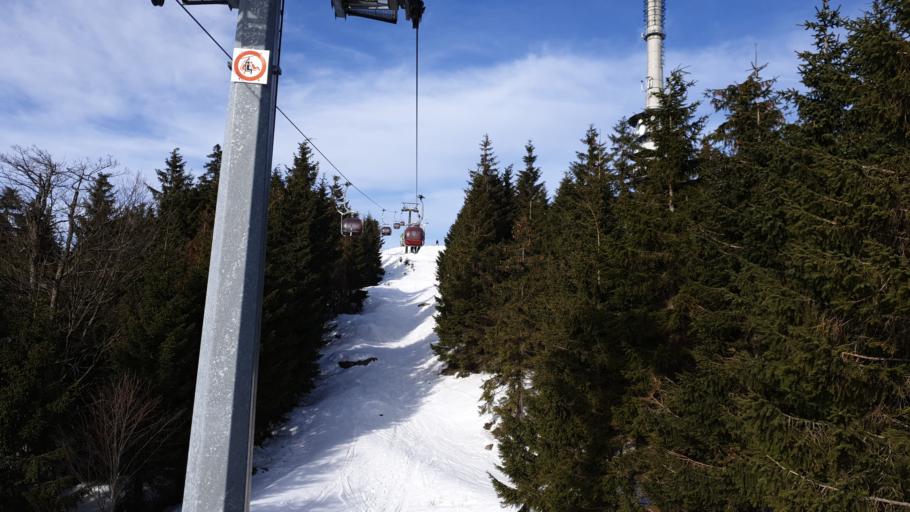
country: DE
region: Bavaria
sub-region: Upper Franconia
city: Bischofsgrun
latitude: 50.0282
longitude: 11.8077
